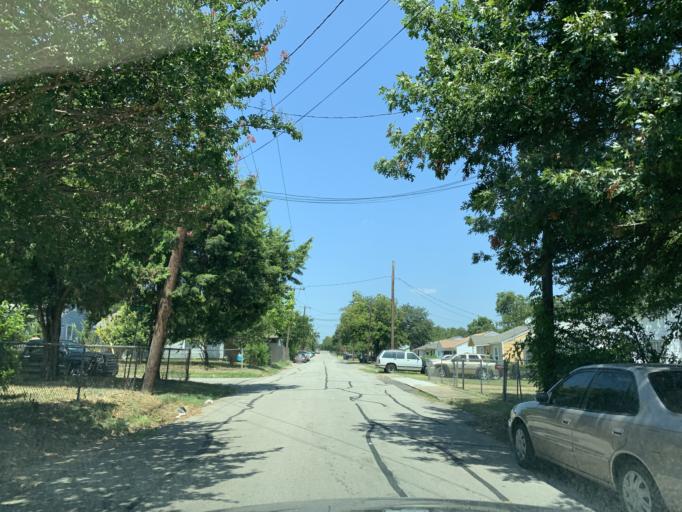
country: US
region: Texas
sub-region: Dallas County
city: Hutchins
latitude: 32.6878
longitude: -96.7970
